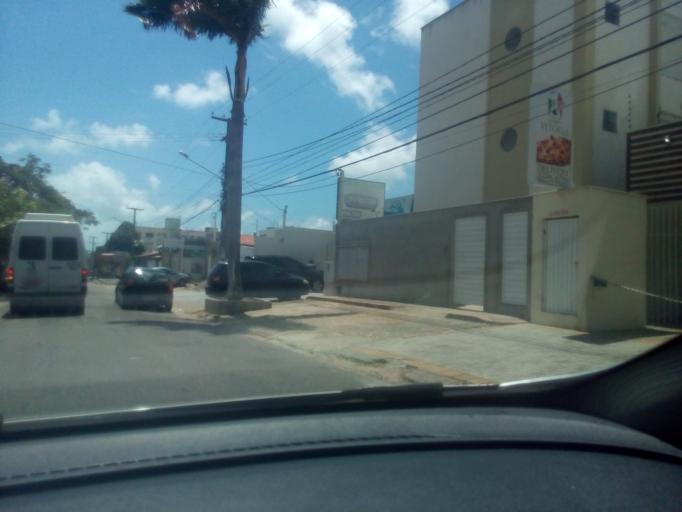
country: BR
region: Rio Grande do Norte
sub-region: Parnamirim
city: Parnamirim
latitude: -5.8791
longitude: -35.2080
